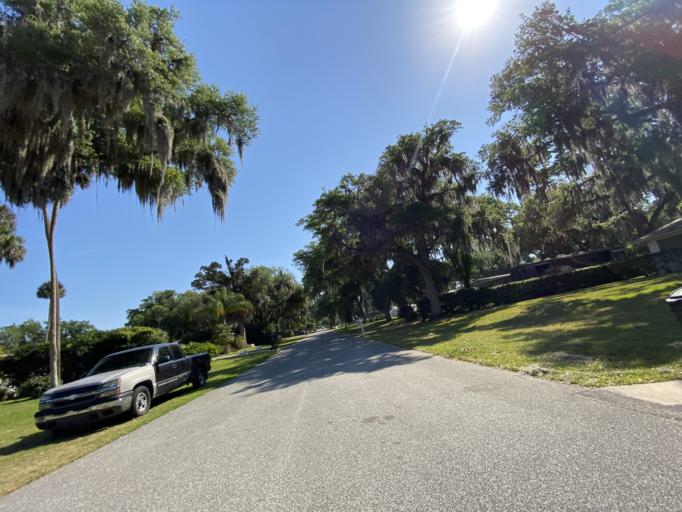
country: US
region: Florida
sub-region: Volusia County
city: South Daytona
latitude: 29.1637
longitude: -81.0149
